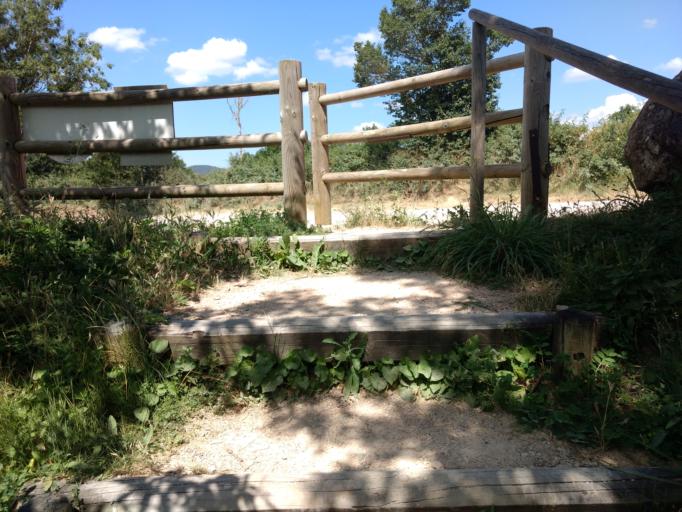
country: FR
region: Midi-Pyrenees
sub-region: Departement de l'Aveyron
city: Severac-le-Chateau
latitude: 44.3252
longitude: 3.0457
